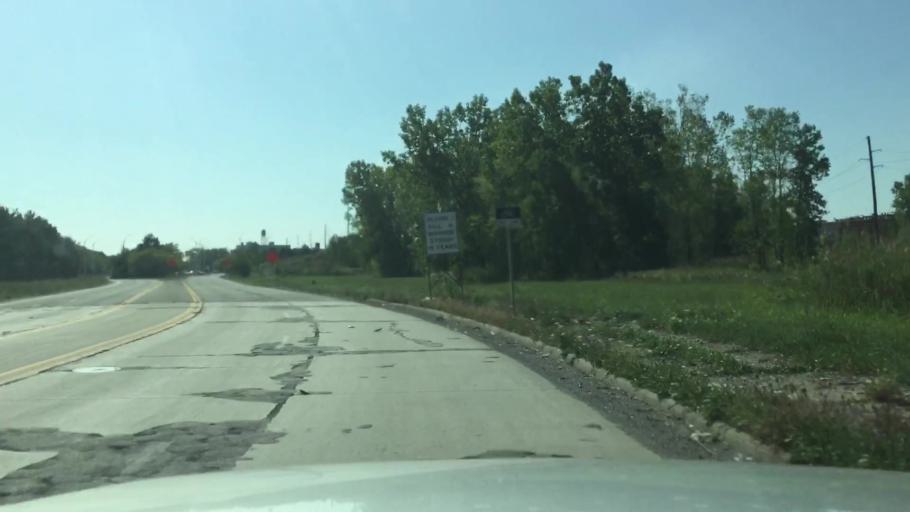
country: US
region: Michigan
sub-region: Wayne County
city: Hamtramck
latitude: 42.3801
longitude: -83.0551
